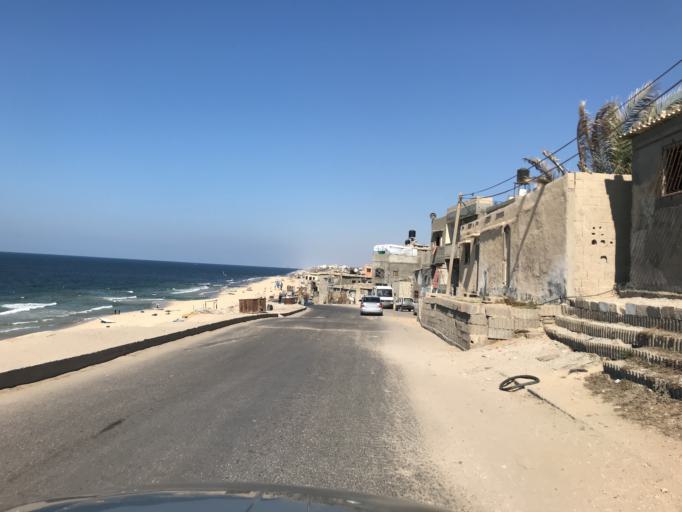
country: PS
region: Gaza Strip
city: Dayr al Balah
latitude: 31.4270
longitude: 34.3400
